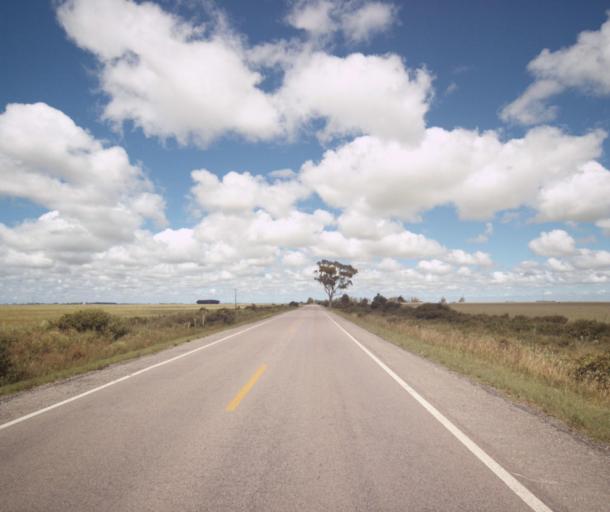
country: BR
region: Rio Grande do Sul
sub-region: Rio Grande
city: Rio Grande
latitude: -32.1720
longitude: -52.4139
